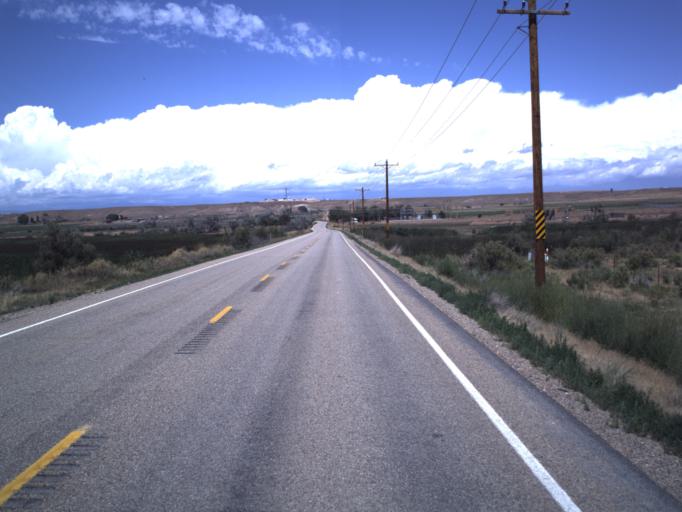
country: US
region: Utah
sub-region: Uintah County
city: Naples
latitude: 40.1970
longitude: -109.6647
